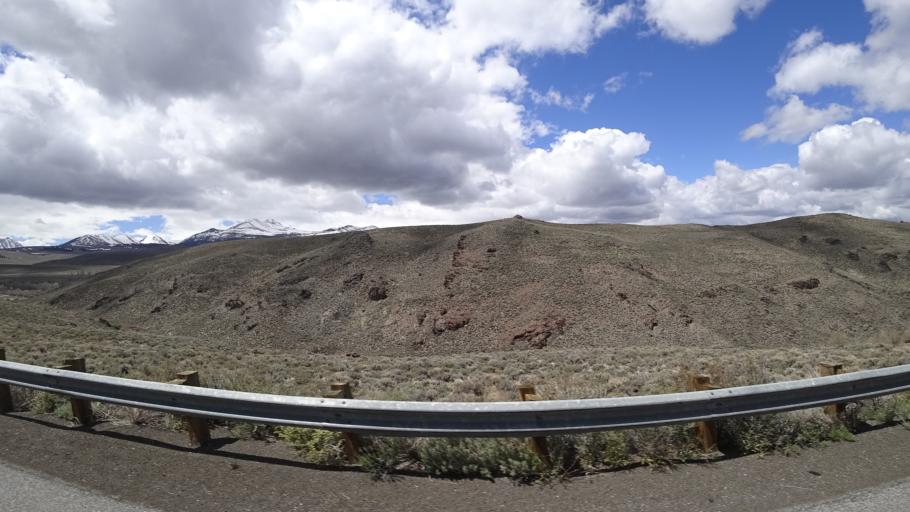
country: US
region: California
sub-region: Mono County
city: Bridgeport
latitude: 38.1256
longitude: -119.1821
